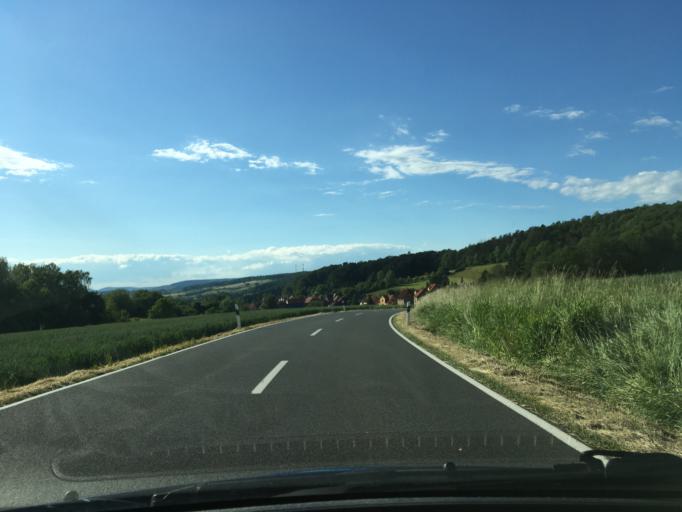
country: DE
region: Lower Saxony
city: Delligsen
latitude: 51.9646
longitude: 9.7708
